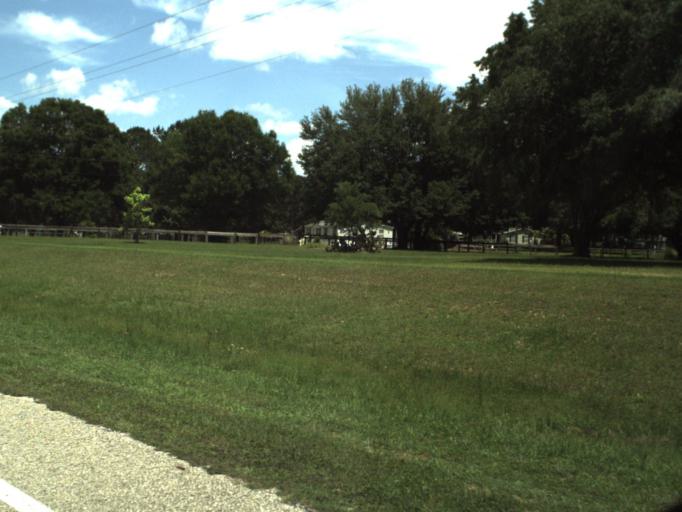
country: US
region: Florida
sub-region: Marion County
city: Citra
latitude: 29.3698
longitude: -82.1718
